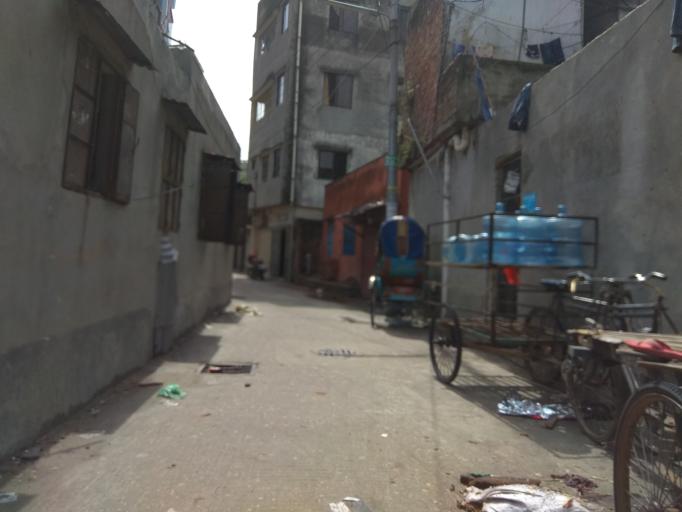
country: BD
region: Dhaka
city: Azimpur
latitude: 23.7972
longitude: 90.3572
